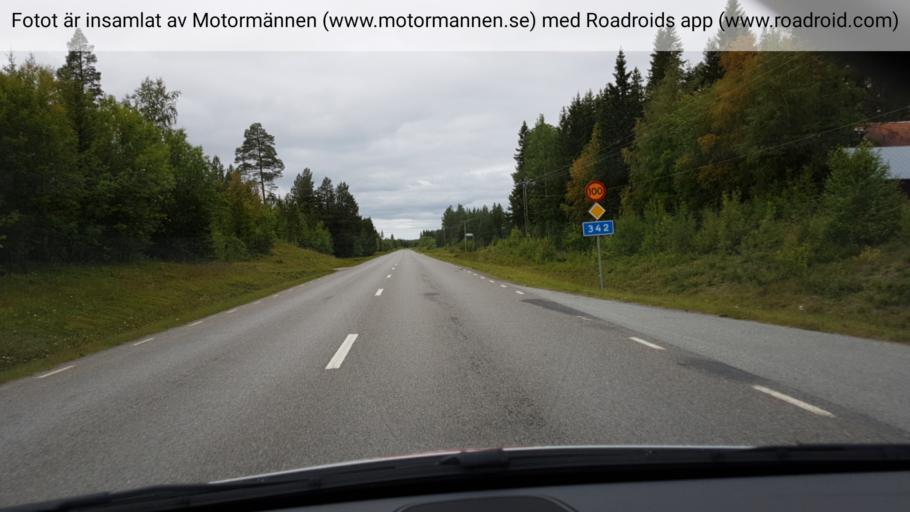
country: SE
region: Jaemtland
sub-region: Stroemsunds Kommun
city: Stroemsund
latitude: 64.2314
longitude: 15.4846
